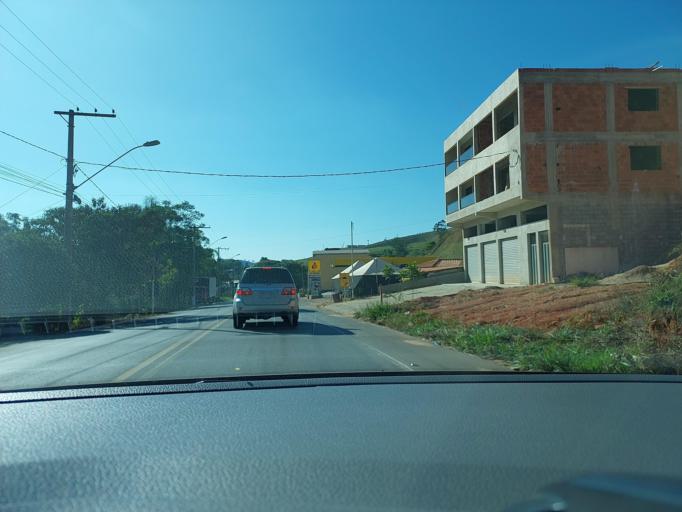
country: BR
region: Minas Gerais
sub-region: Vicosa
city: Vicosa
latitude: -20.6686
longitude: -42.8553
